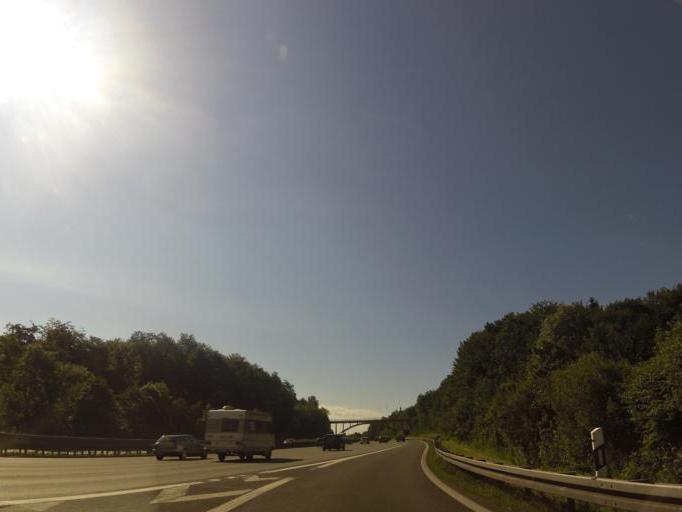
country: DE
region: Baden-Wuerttemberg
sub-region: Regierungsbezirk Stuttgart
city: Sindelfingen
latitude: 48.7405
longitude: 9.0358
